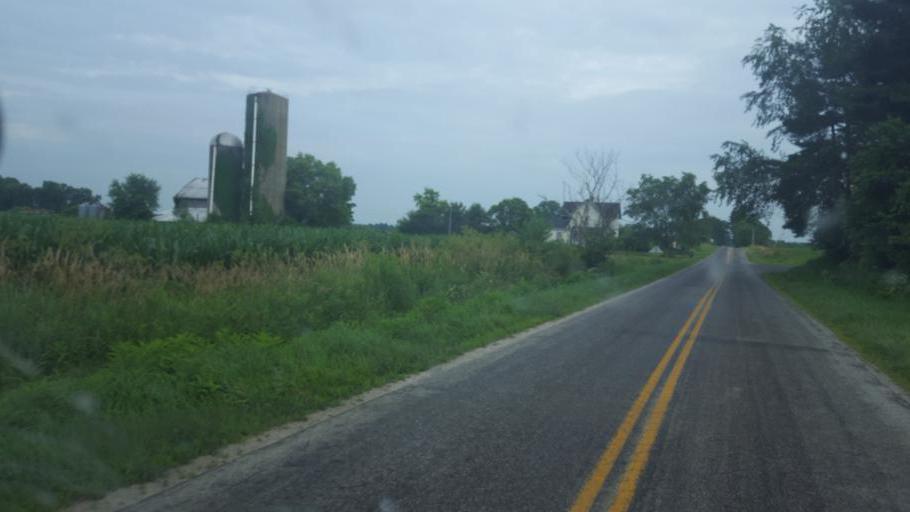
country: US
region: Ohio
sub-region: Ashland County
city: Loudonville
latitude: 40.7708
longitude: -82.1567
